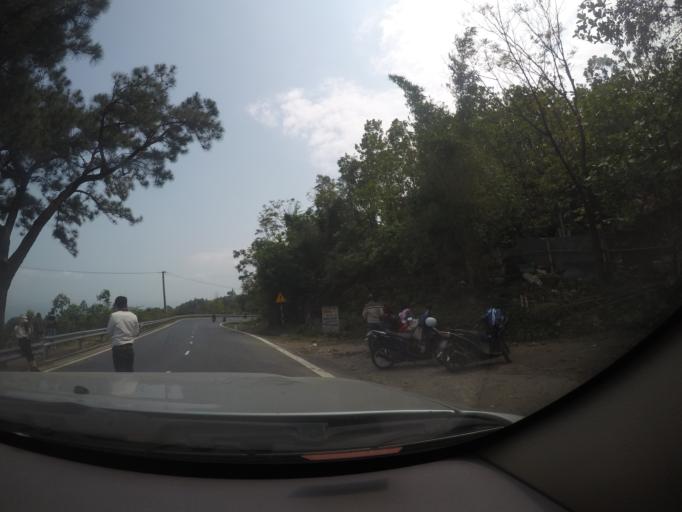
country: VN
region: Da Nang
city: Lien Chieu
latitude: 16.1689
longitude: 108.1262
